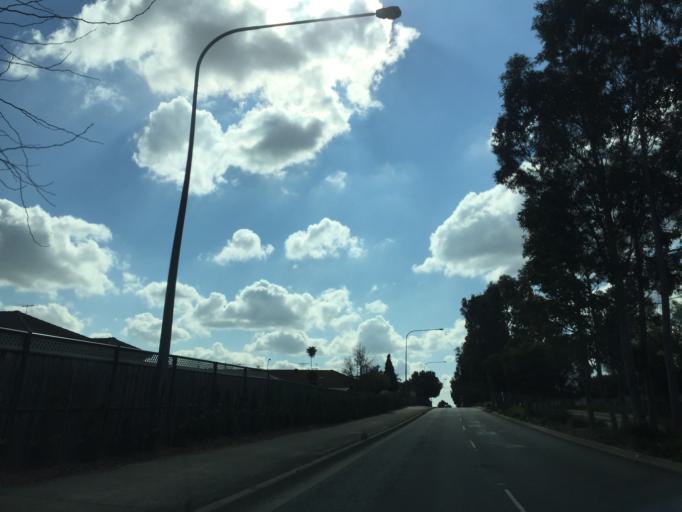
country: AU
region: New South Wales
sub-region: Blacktown
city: Quakers Hill
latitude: -33.7158
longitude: 150.8927
